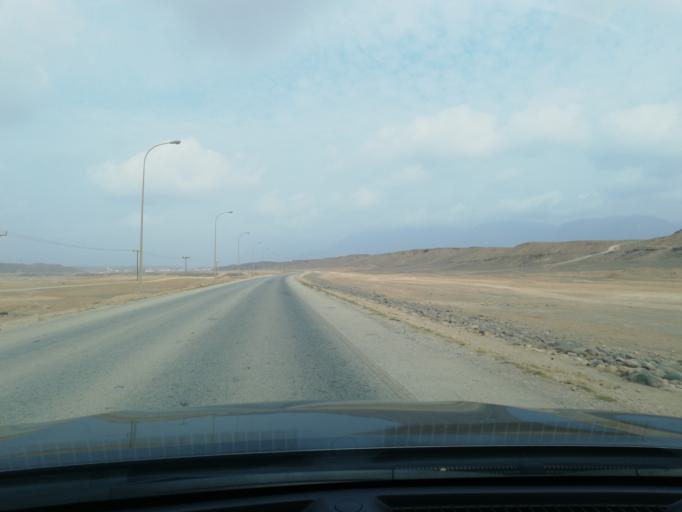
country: OM
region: Zufar
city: Salalah
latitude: 16.9591
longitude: 53.8955
